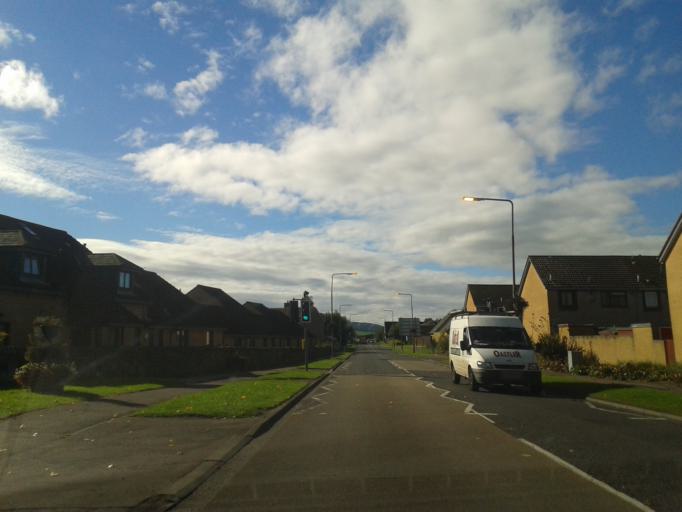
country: GB
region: Scotland
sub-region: Fife
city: Leuchars
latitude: 56.3819
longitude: -2.8873
